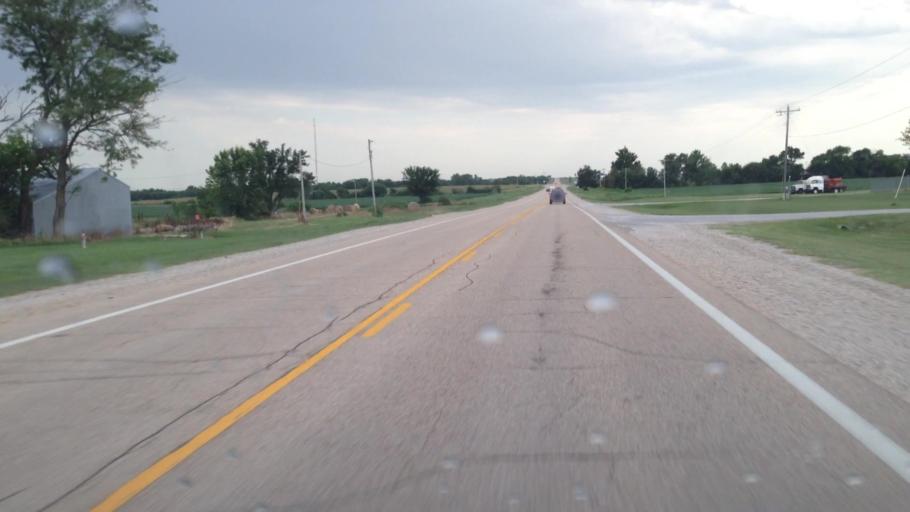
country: US
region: Kansas
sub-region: Coffey County
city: Burlington
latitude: 38.1779
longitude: -95.7388
